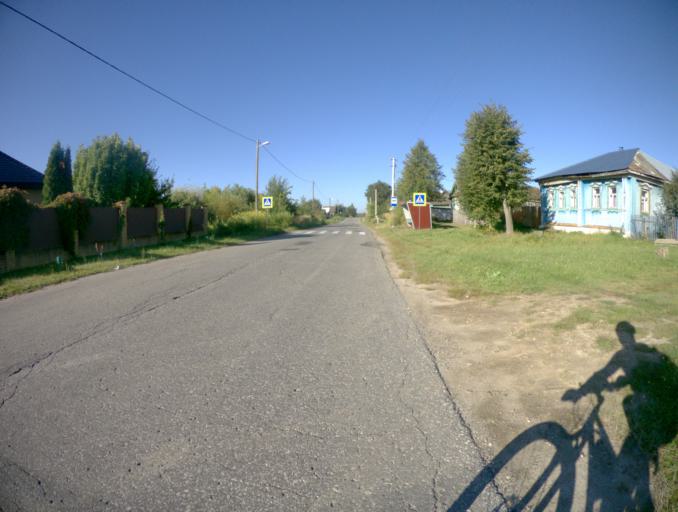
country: RU
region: Vladimir
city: Luknovo
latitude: 56.2136
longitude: 42.0069
